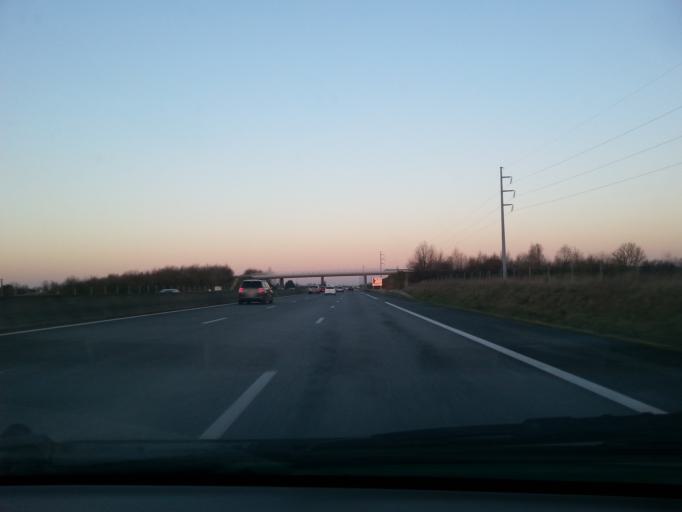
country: FR
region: Centre
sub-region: Departement d'Eure-et-Loir
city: Dammarie
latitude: 48.3520
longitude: 1.4250
